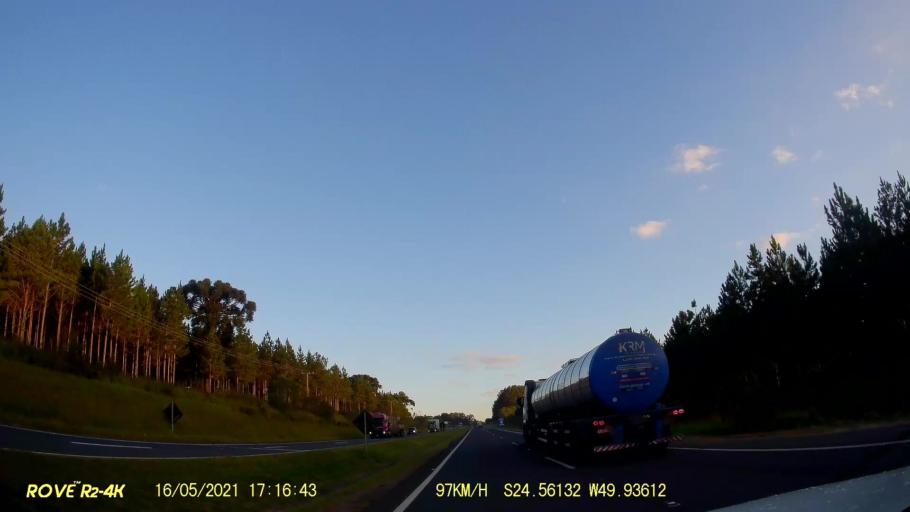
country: BR
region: Parana
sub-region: Pirai Do Sul
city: Pirai do Sul
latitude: -24.5616
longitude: -49.9362
